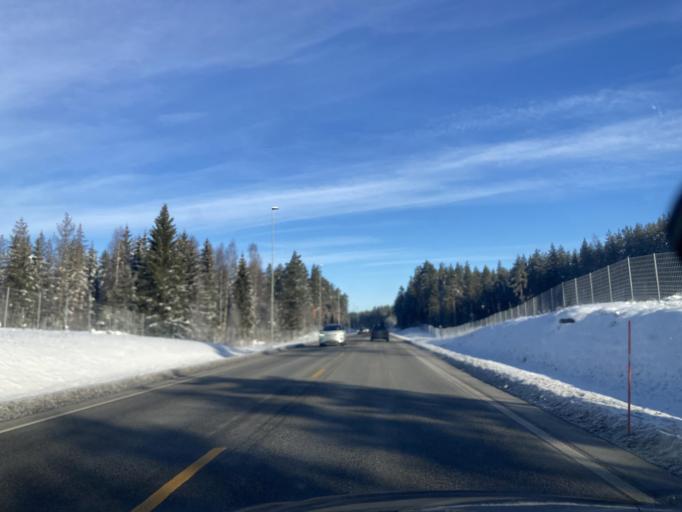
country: NO
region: Hedmark
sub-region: Loten
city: Loten
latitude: 60.7598
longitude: 11.3069
